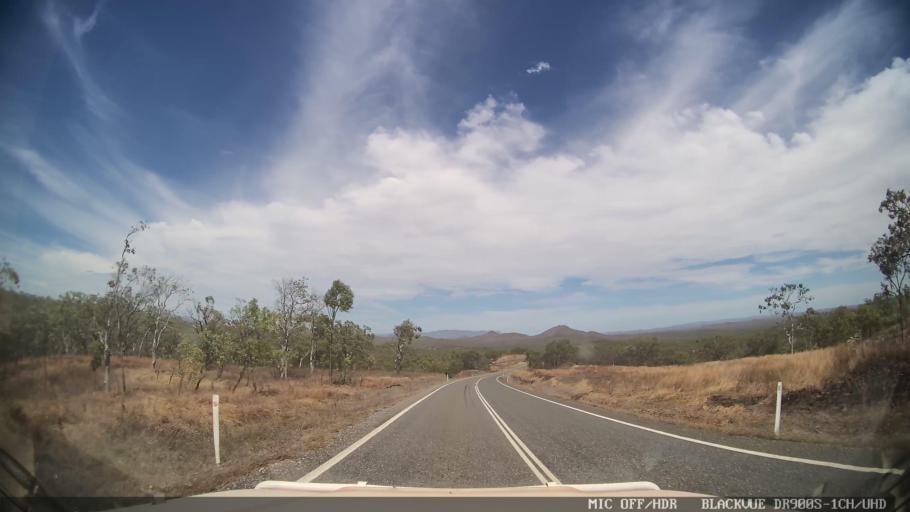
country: AU
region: Queensland
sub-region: Cook
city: Cooktown
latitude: -16.0225
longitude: 144.8117
